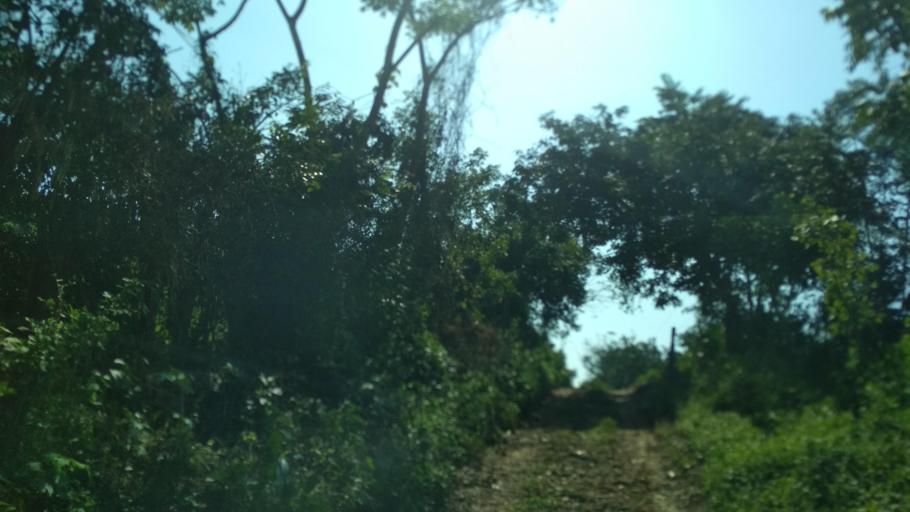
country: MX
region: Puebla
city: San Jose Acateno
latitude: 20.1774
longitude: -97.2272
